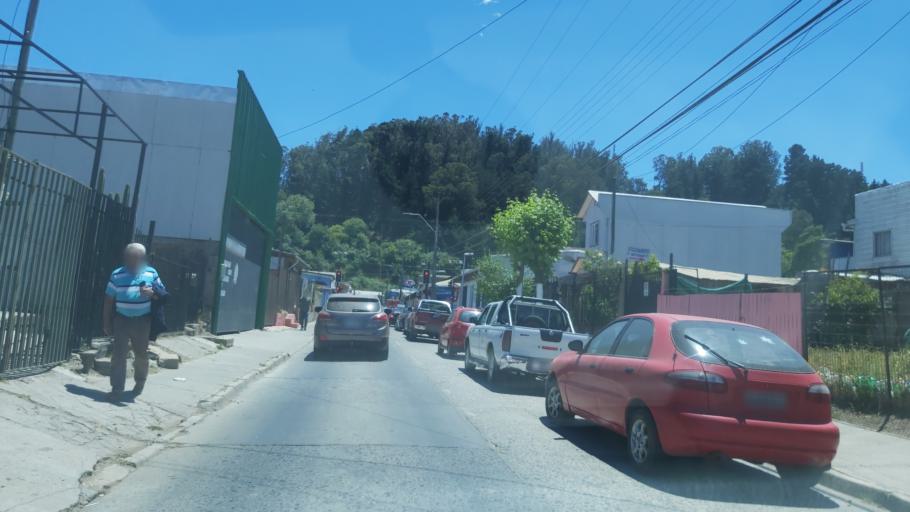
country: CL
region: Maule
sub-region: Provincia de Talca
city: Constitucion
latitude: -35.3270
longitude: -72.4125
